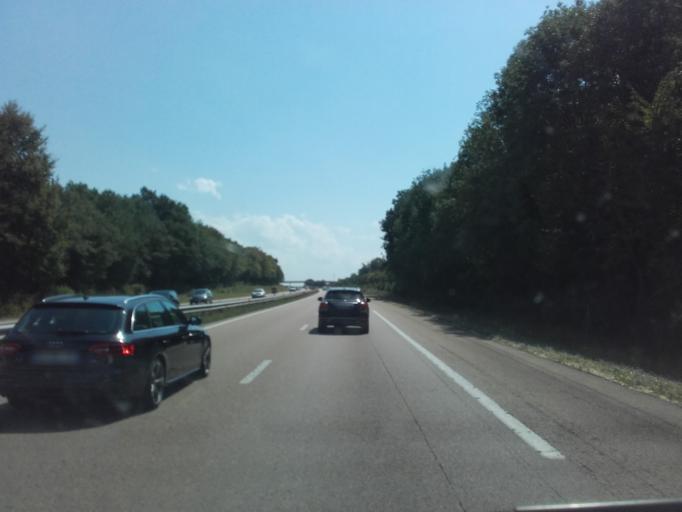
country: FR
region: Bourgogne
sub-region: Departement de l'Yonne
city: Joux-la-Ville
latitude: 47.6338
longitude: 3.9065
